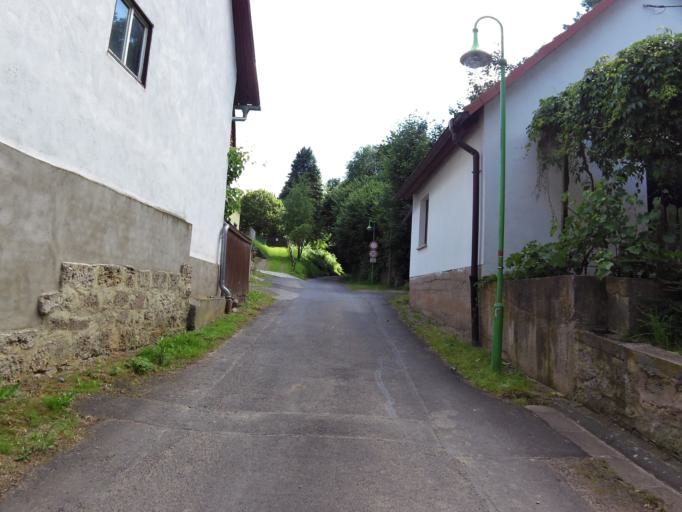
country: DE
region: Hesse
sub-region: Regierungsbezirk Kassel
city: Herleshausen
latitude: 50.9938
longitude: 10.1904
